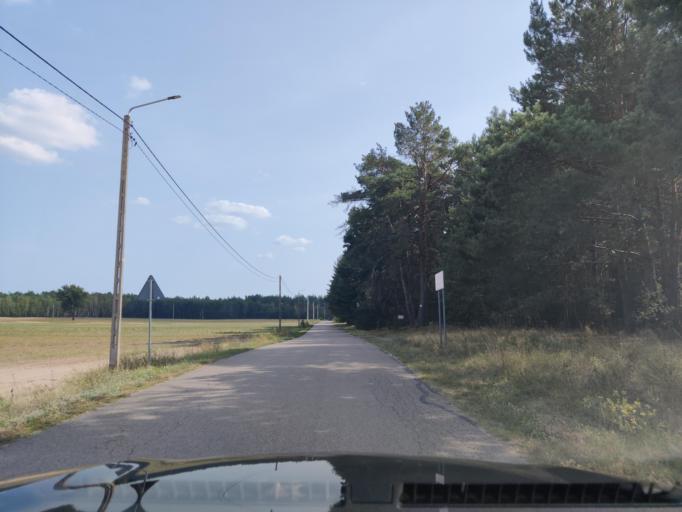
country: PL
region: Masovian Voivodeship
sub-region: Powiat makowski
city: Rozan
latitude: 52.8614
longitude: 21.4469
